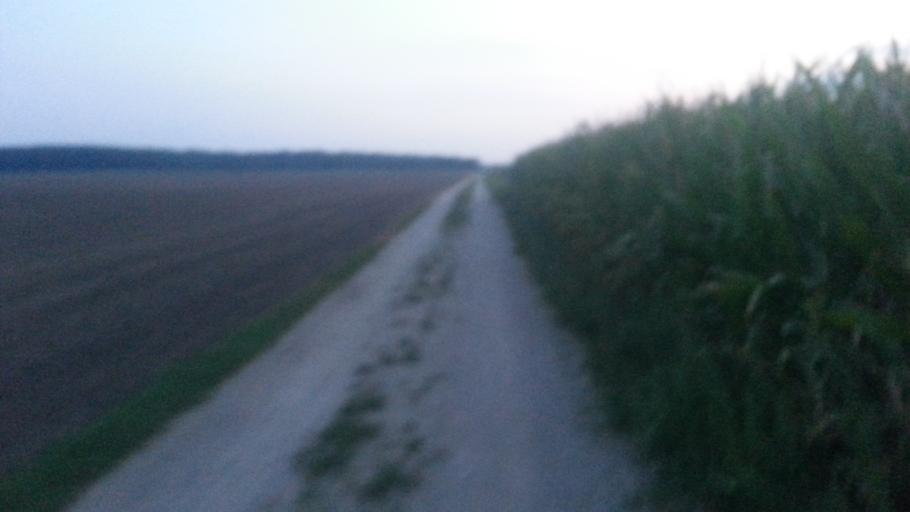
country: DE
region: Bavaria
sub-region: Upper Bavaria
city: Neufahrn bei Freising
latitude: 48.3069
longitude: 11.6545
